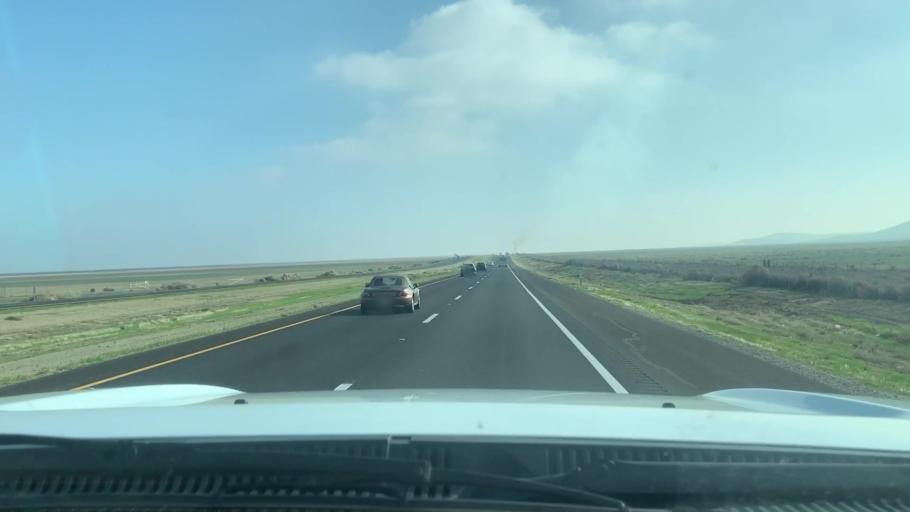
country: US
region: California
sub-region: Kern County
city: Lost Hills
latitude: 35.6370
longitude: -120.0118
